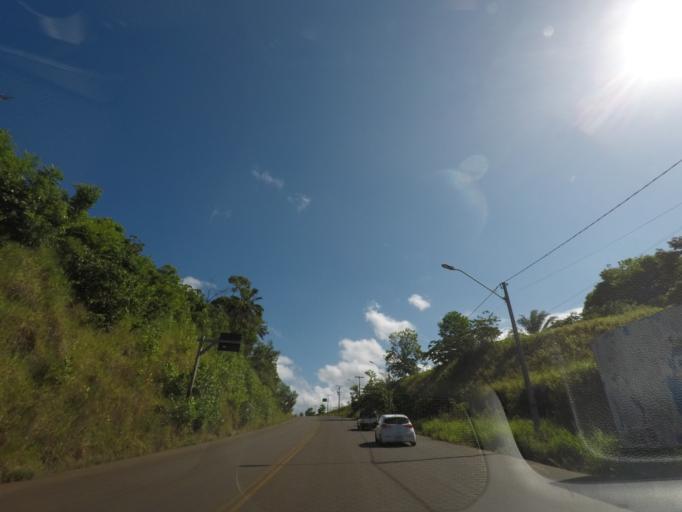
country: BR
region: Bahia
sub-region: Camamu
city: Camamu
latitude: -13.9498
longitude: -39.1073
